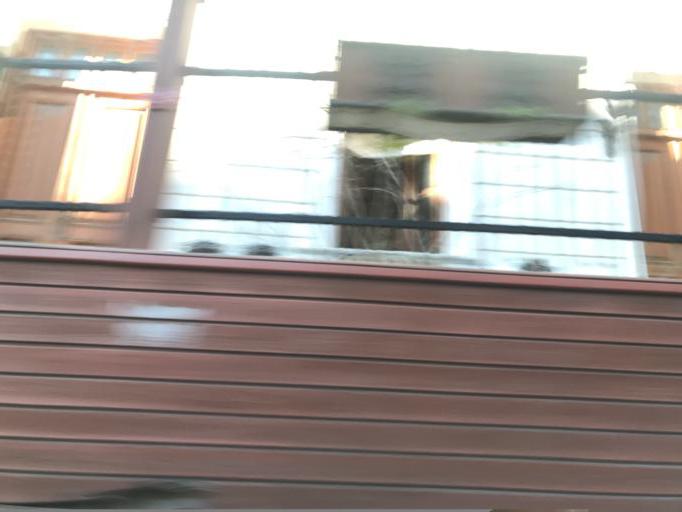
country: TR
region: Istanbul
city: Bahcelievler
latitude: 40.9622
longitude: 28.8249
